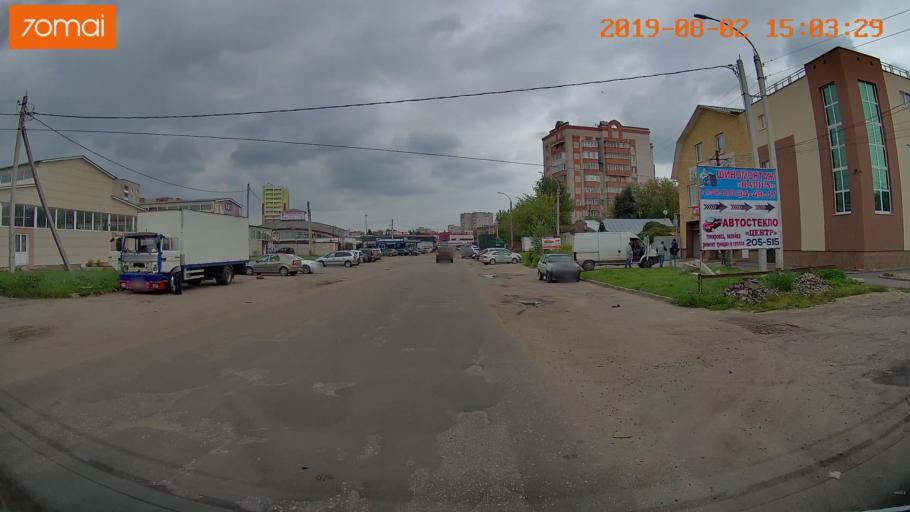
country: RU
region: Ivanovo
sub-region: Gorod Ivanovo
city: Ivanovo
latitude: 56.9904
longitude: 40.9655
